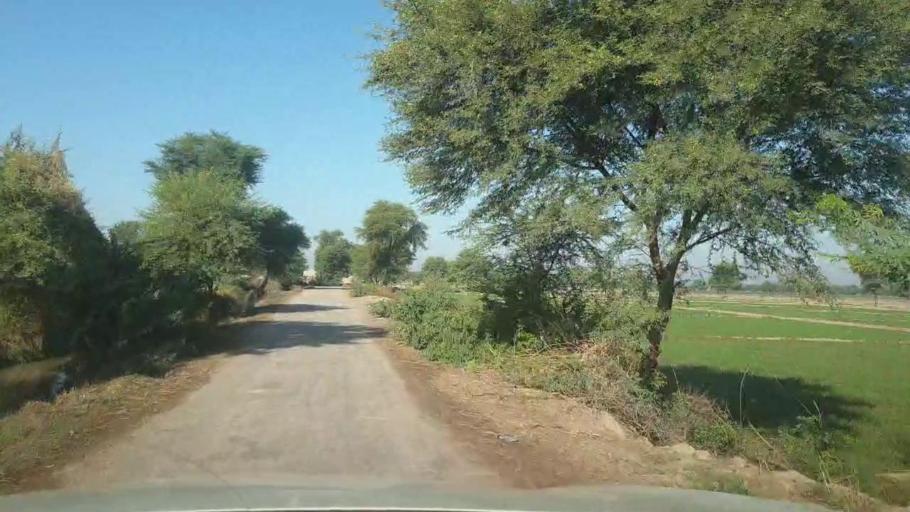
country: PK
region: Sindh
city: Bhan
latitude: 26.5463
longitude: 67.6722
